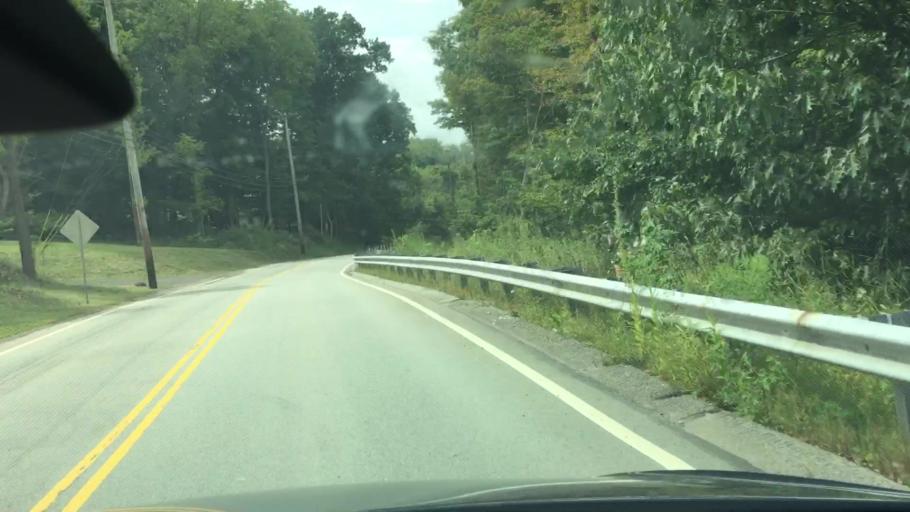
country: US
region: Pennsylvania
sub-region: Allegheny County
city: Monroeville
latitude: 40.4295
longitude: -79.7632
